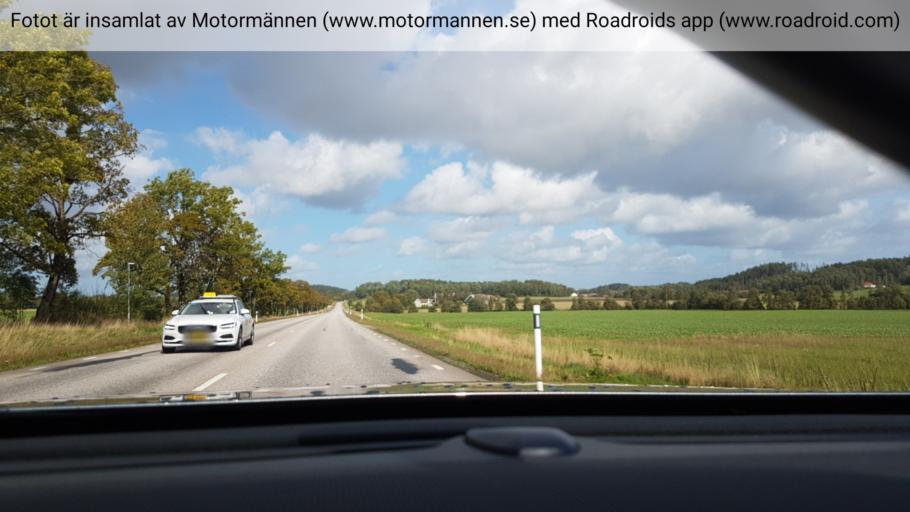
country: SE
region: Vaestra Goetaland
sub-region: Alingsas Kommun
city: Sollebrunn
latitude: 58.0922
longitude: 12.4995
